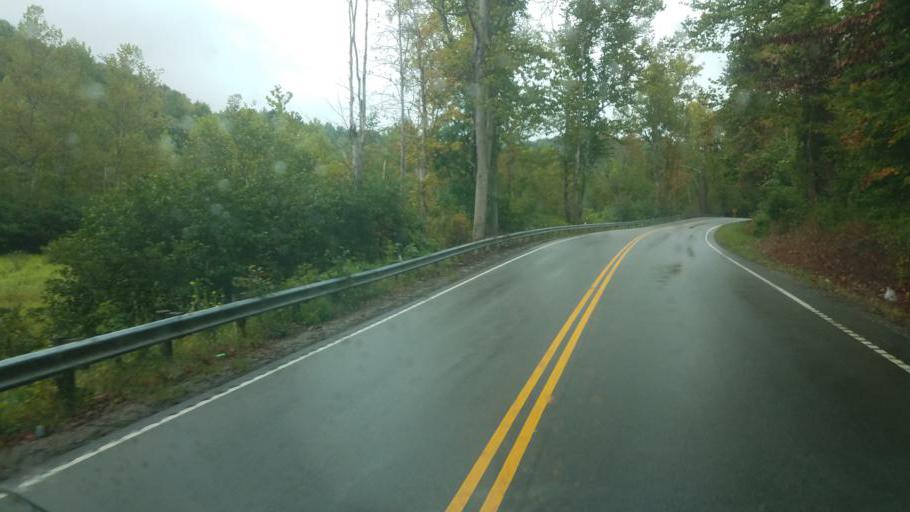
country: US
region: Ohio
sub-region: Jackson County
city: Oak Hill
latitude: 38.8373
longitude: -82.6479
